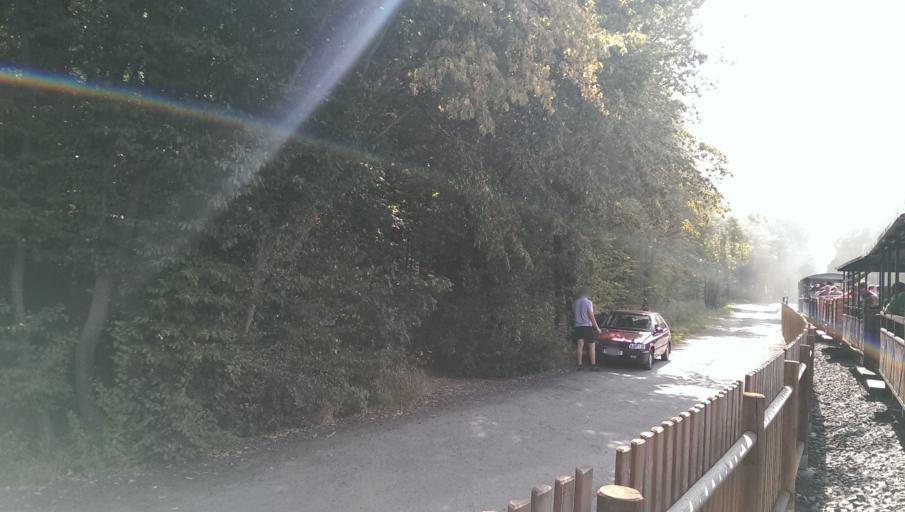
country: CZ
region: Central Bohemia
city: Stary Kolin
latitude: 50.0617
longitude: 15.2716
